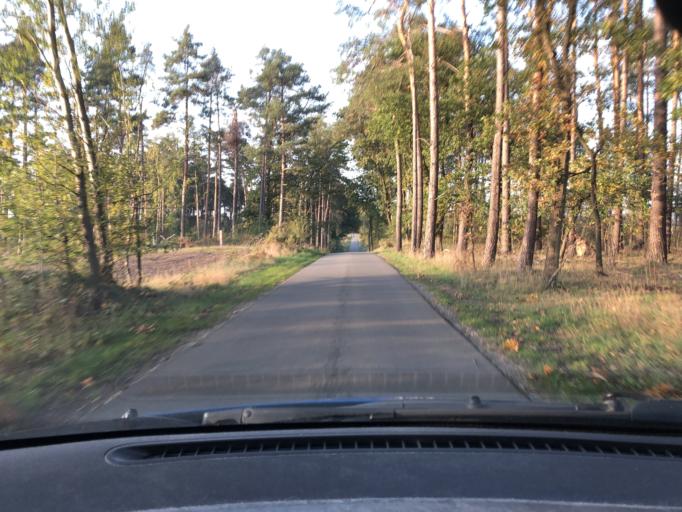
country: DE
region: Lower Saxony
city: Hitzacker
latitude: 53.1327
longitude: 11.0090
